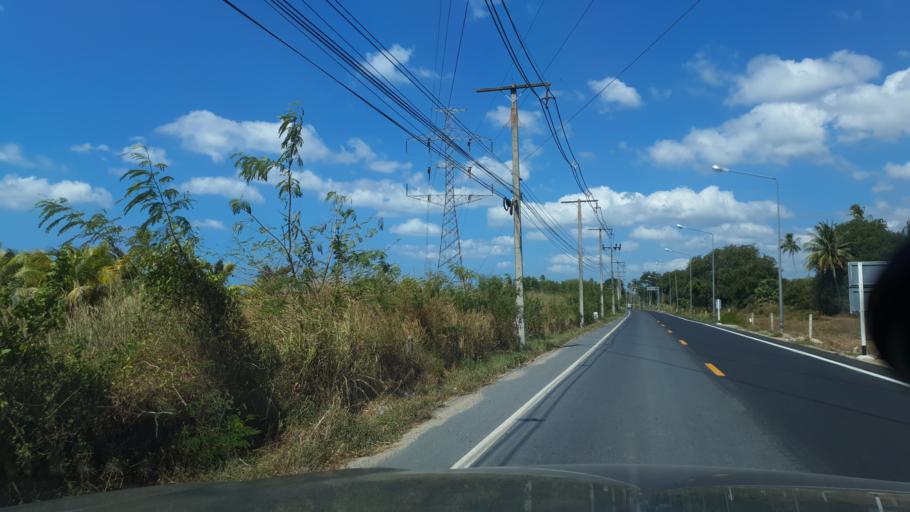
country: TH
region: Phuket
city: Thalang
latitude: 8.1506
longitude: 98.3056
